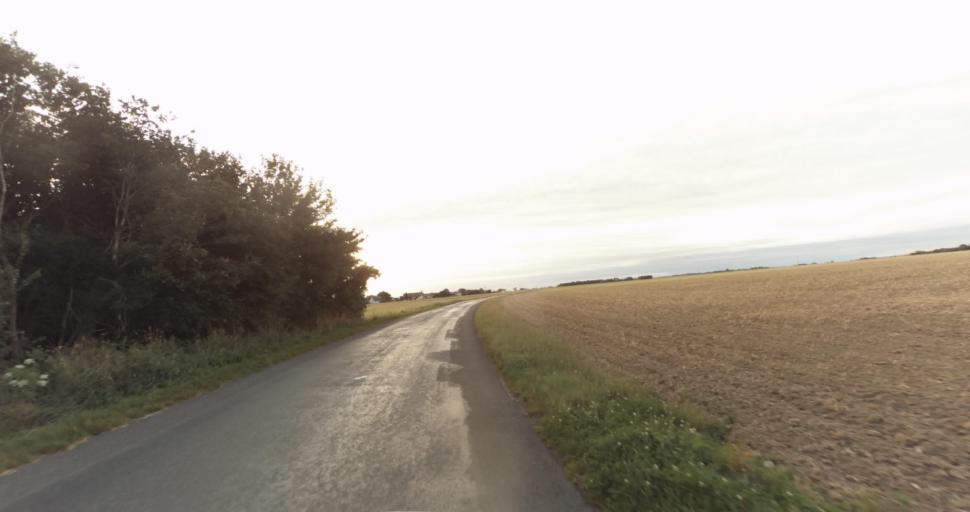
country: FR
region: Haute-Normandie
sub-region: Departement de l'Eure
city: La Madeleine-de-Nonancourt
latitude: 48.8690
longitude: 1.2235
